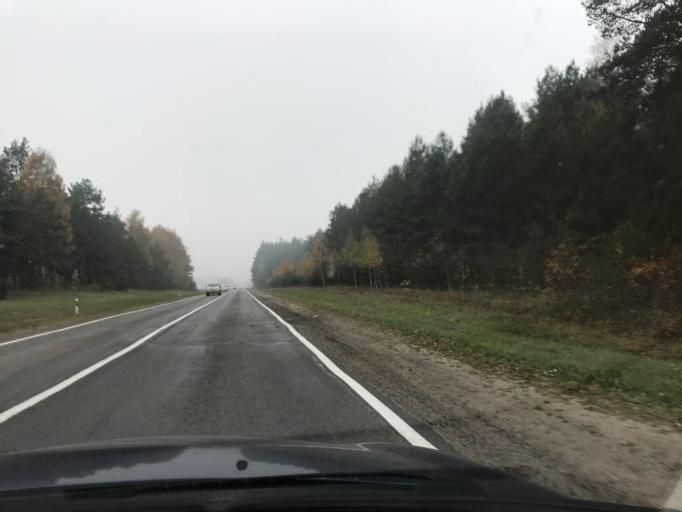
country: BY
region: Grodnenskaya
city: Hrodna
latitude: 53.7825
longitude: 23.8499
